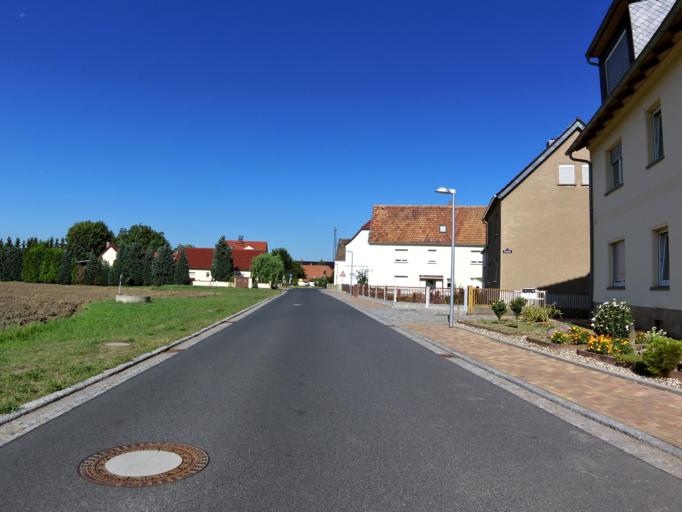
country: DE
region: Saxony
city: Riesa
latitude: 51.3428
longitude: 13.2934
